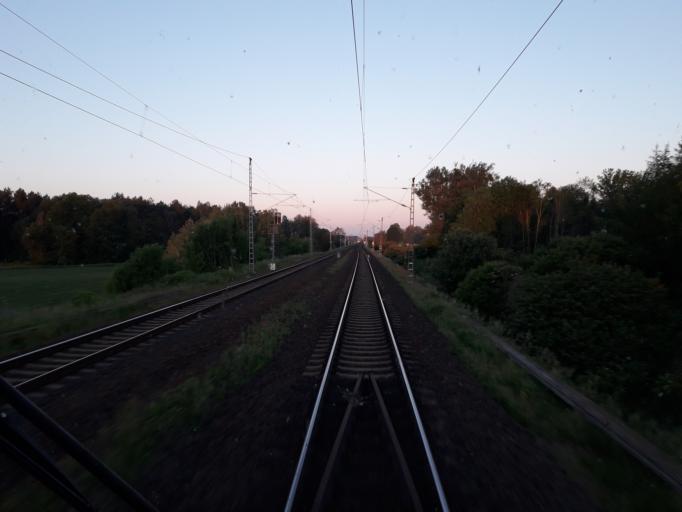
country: DE
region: Brandenburg
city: Falkensee
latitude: 52.6068
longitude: 13.0726
